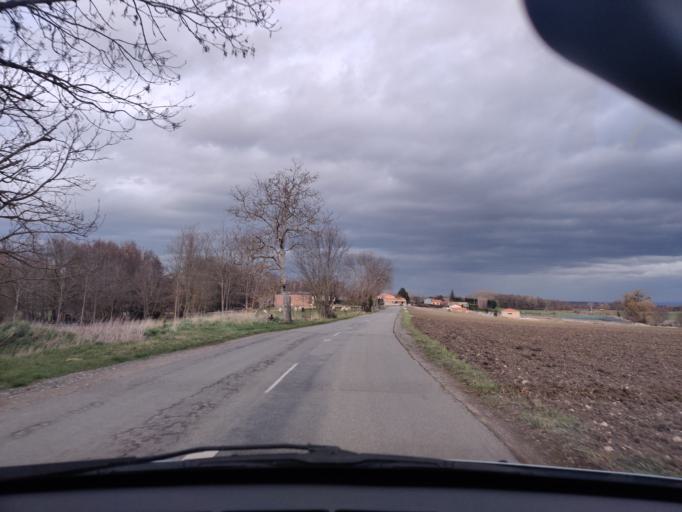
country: FR
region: Auvergne
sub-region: Departement du Puy-de-Dome
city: Saint-Bonnet-pres-Riom
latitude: 45.9416
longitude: 3.1064
